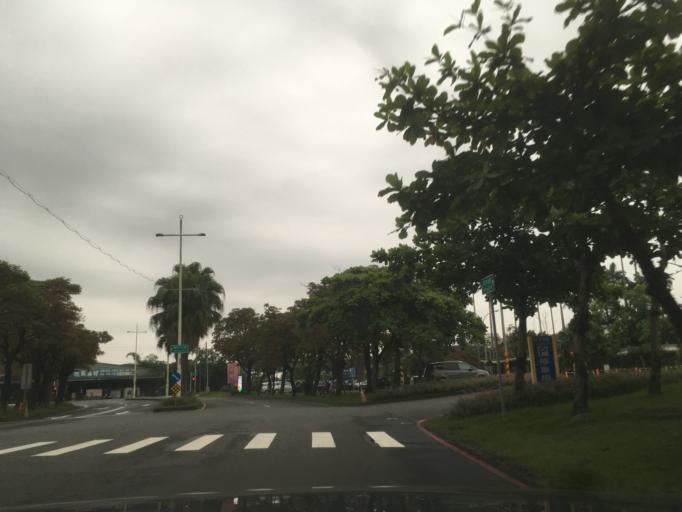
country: TW
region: Taiwan
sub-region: Yilan
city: Yilan
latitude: 24.7315
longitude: 121.7633
